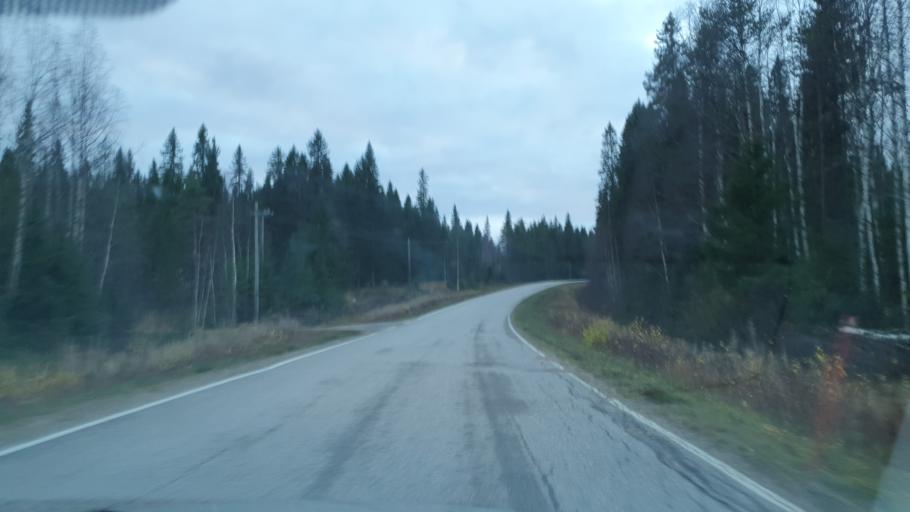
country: FI
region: Kainuu
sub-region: Kajaani
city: Ristijaervi
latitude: 64.4280
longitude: 28.3797
